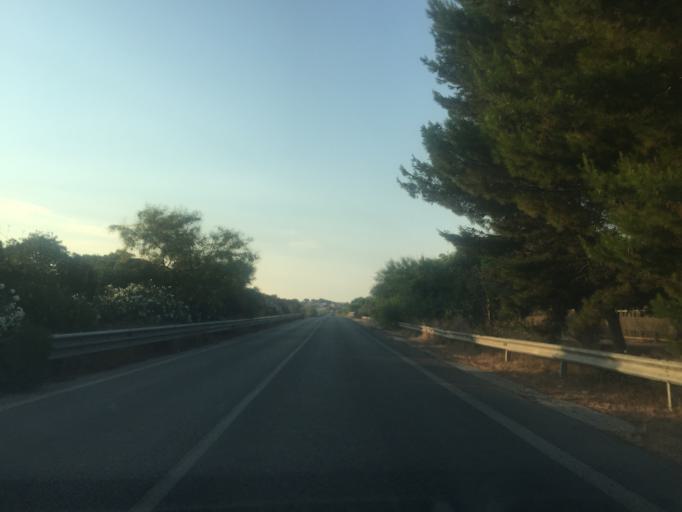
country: IT
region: Sicily
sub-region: Ragusa
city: Cava d'Aliga
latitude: 36.7214
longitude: 14.7520
